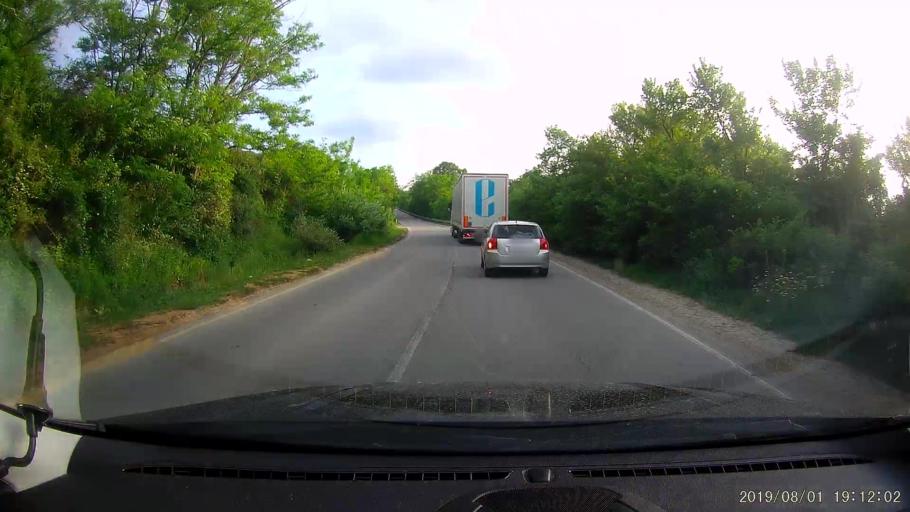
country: BG
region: Shumen
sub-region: Obshtina Smyadovo
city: Smyadovo
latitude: 42.9680
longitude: 26.9534
